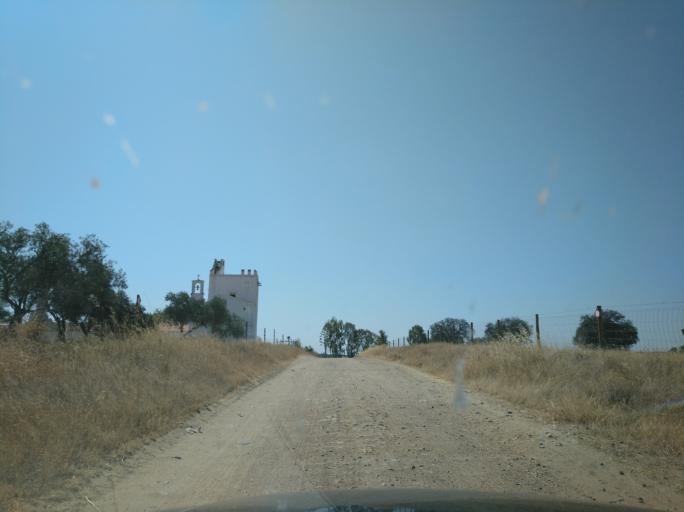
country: PT
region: Portalegre
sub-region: Campo Maior
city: Campo Maior
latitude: 39.0223
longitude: -6.9782
